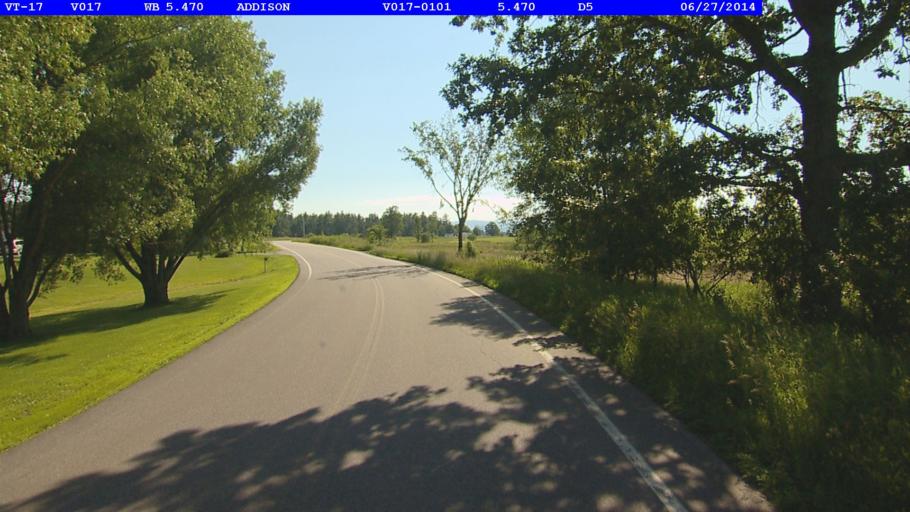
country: US
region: New York
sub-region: Essex County
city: Port Henry
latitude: 44.0836
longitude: -73.3603
